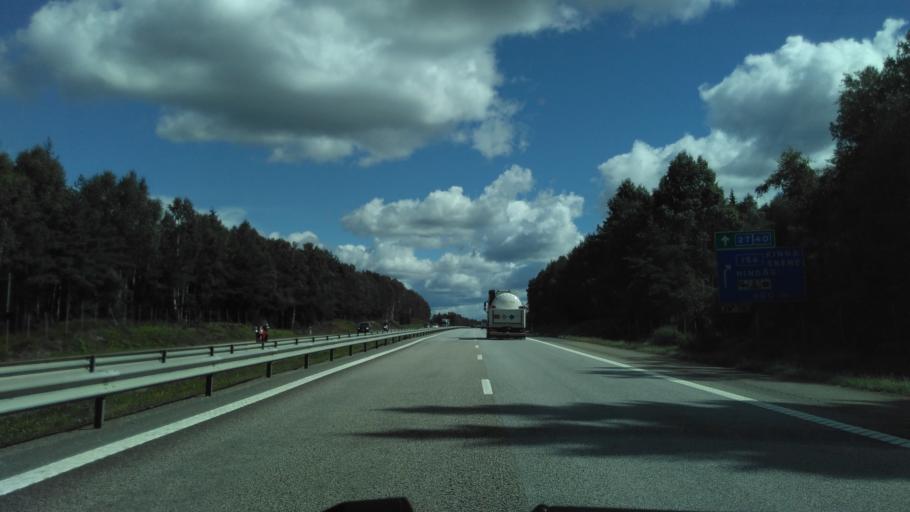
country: SE
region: Vaestra Goetaland
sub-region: Harryda Kommun
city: Hindas
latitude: 57.6773
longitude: 12.3390
